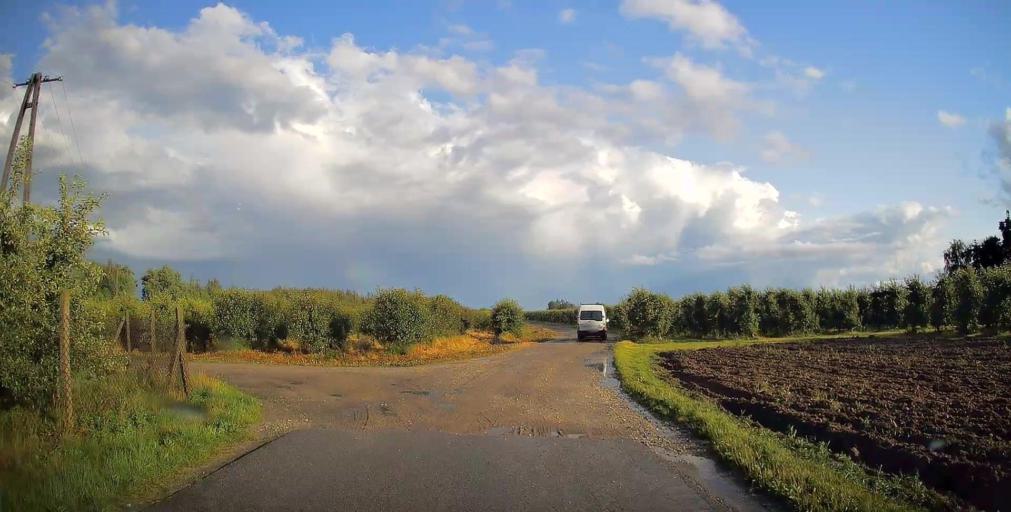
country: PL
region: Masovian Voivodeship
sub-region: Powiat grojecki
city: Goszczyn
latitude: 51.7490
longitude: 20.8859
